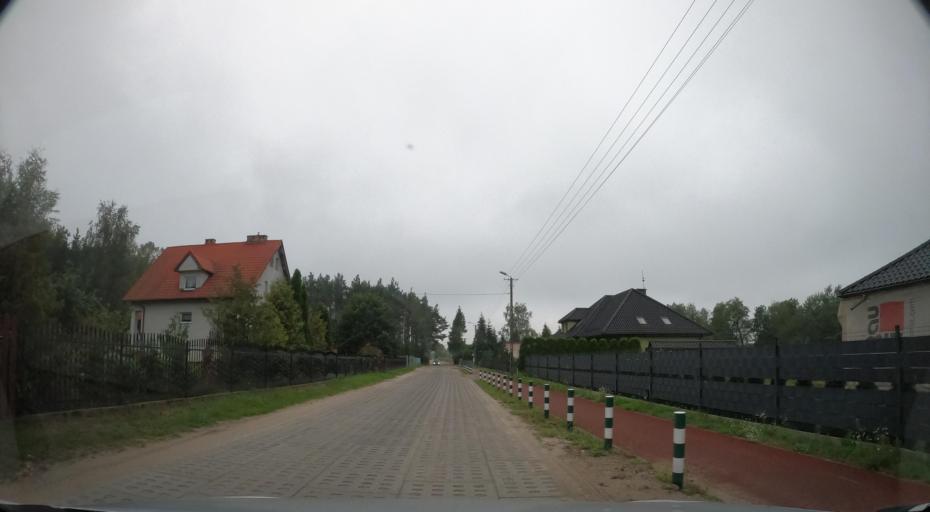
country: PL
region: Pomeranian Voivodeship
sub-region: Powiat kartuski
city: Chwaszczyno
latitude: 54.4315
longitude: 18.4170
